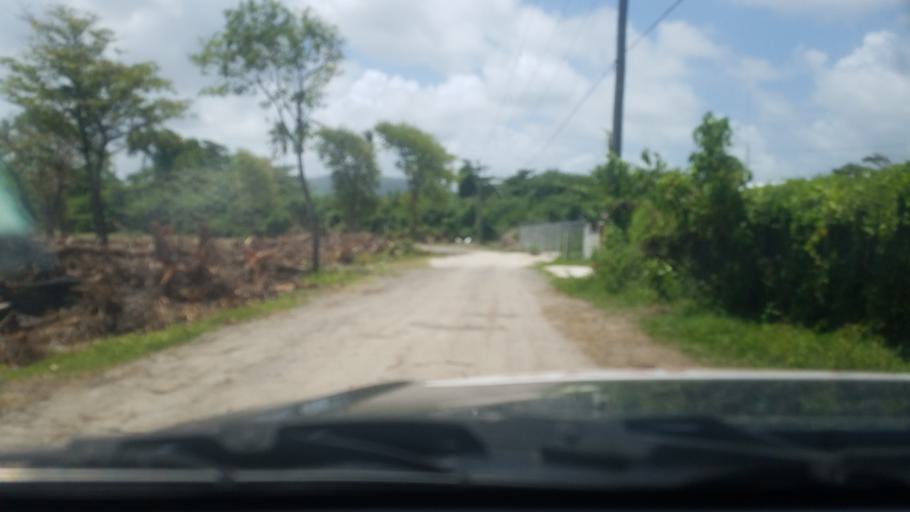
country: LC
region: Vieux-Fort
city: Vieux Fort
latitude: 13.7424
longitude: -60.9422
